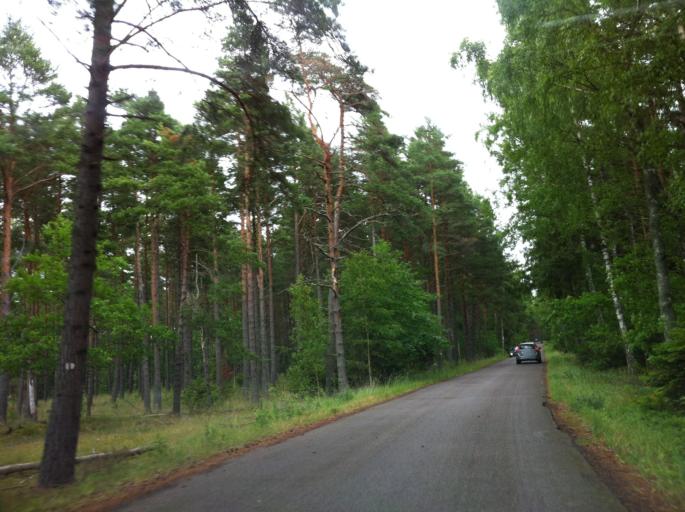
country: SE
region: Kalmar
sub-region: Vasterviks Kommun
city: Vaestervik
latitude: 57.3330
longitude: 17.1015
